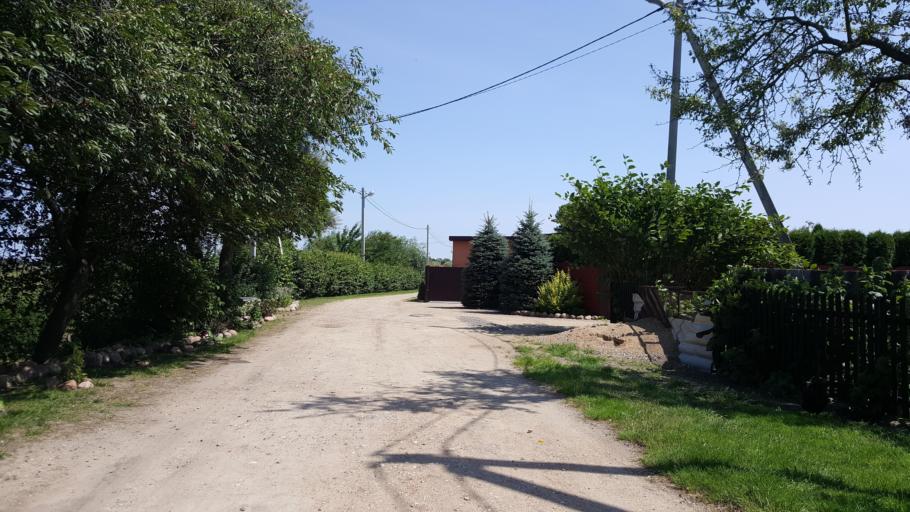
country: BY
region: Brest
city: Vysokaye
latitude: 52.3674
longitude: 23.3910
